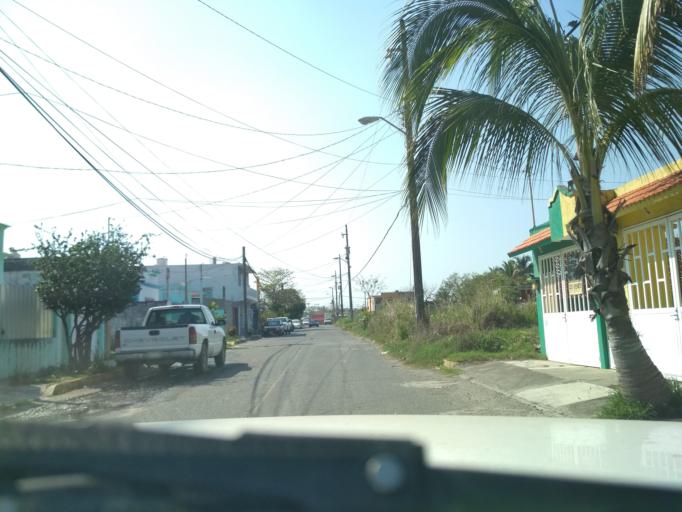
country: MX
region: Veracruz
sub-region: Veracruz
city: Colonia el Renacimiento
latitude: 19.2176
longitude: -96.2130
